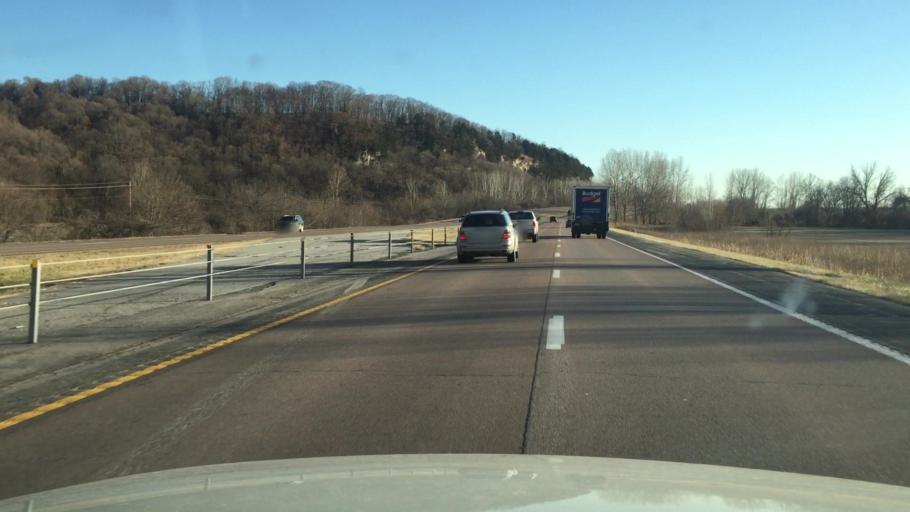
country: US
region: Missouri
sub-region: Cole County
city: Jefferson City
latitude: 38.6396
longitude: -92.1986
